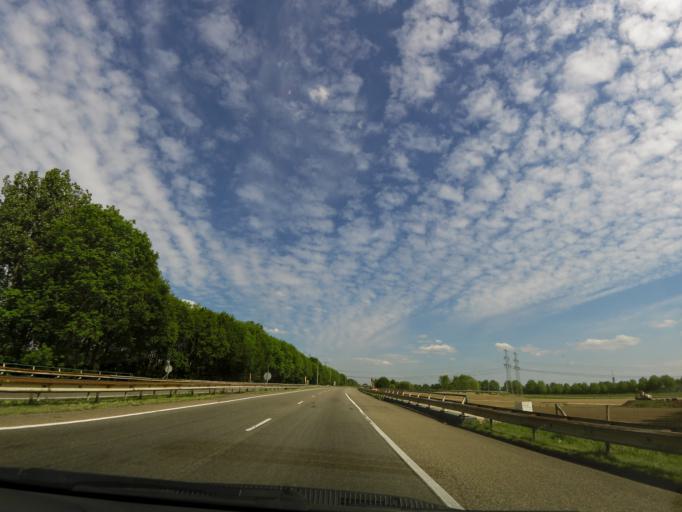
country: NL
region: Limburg
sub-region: Gemeente Leudal
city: Haelen
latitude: 51.2039
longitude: 5.9442
